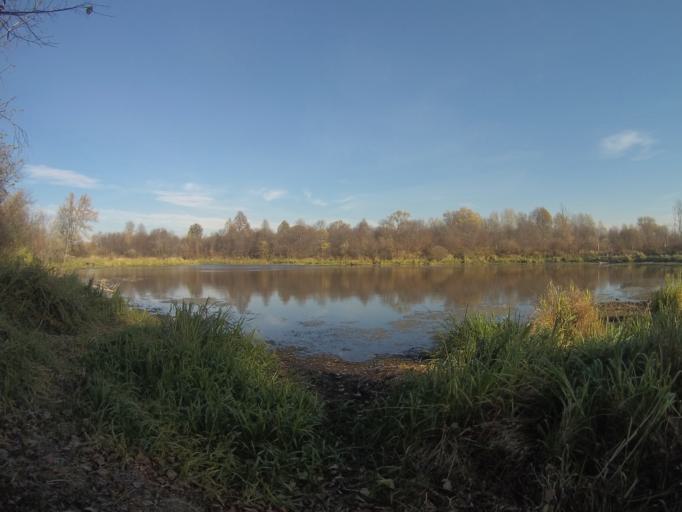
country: RU
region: Vladimir
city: Orgtrud
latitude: 56.1894
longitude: 40.5713
